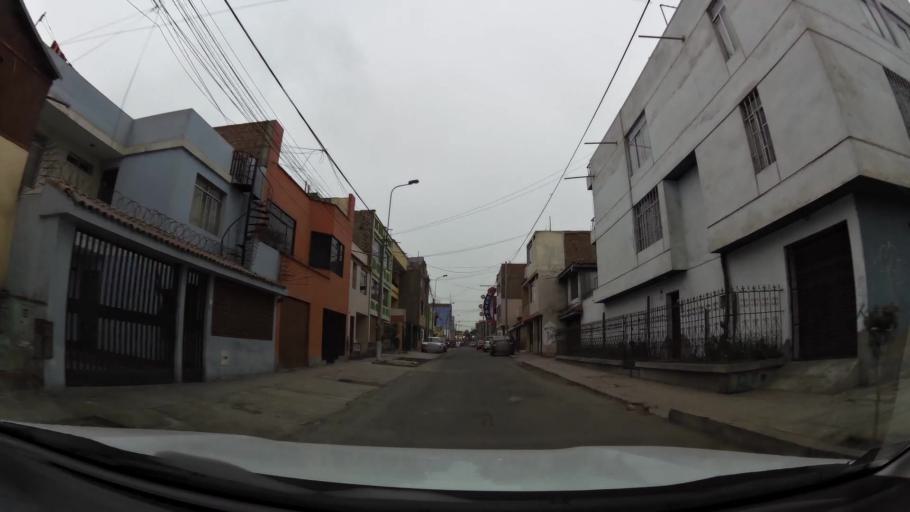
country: PE
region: Lima
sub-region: Lima
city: Surco
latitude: -12.1670
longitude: -76.9720
